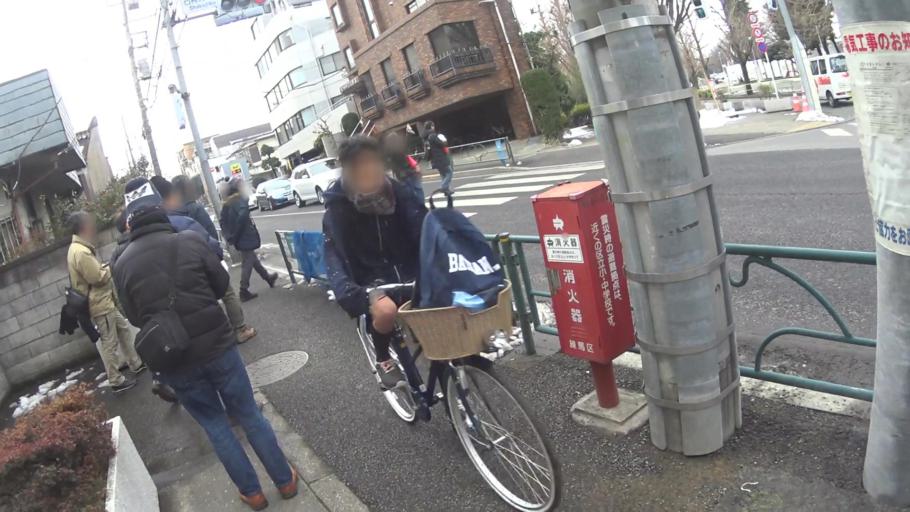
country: JP
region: Tokyo
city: Musashino
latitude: 35.7345
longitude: 139.6000
